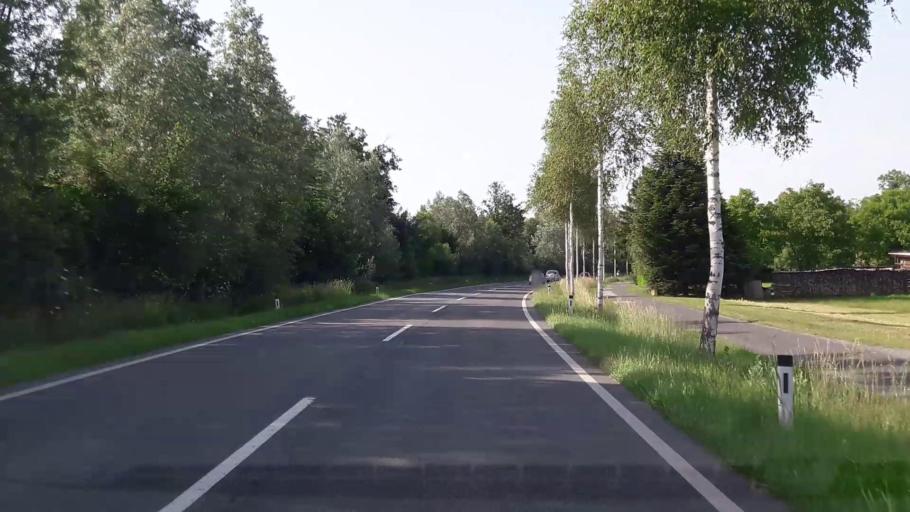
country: AT
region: Burgenland
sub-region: Politischer Bezirk Oberwart
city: Litzelsdorf
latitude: 47.2058
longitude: 16.1597
